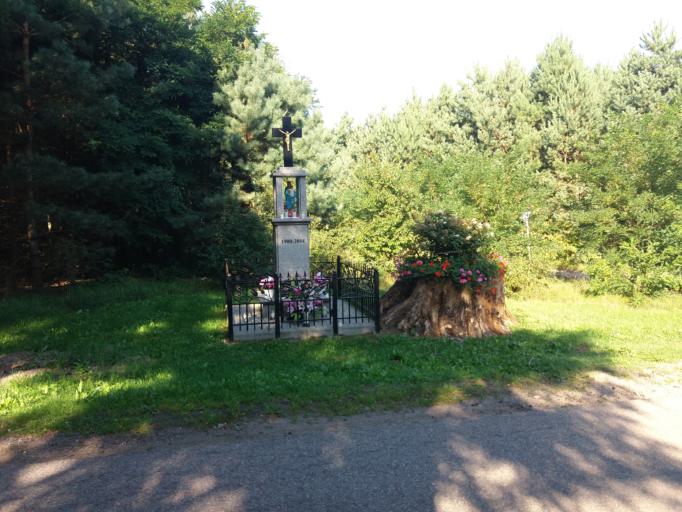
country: PL
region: Masovian Voivodeship
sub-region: Powiat mlawski
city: Mlawa
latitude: 53.1631
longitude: 20.3630
